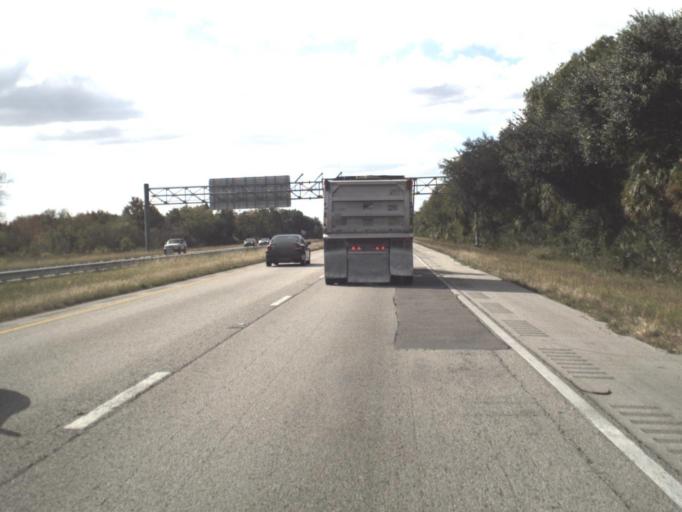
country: US
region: Florida
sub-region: Brevard County
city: Port Saint John
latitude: 28.4530
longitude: -80.8831
